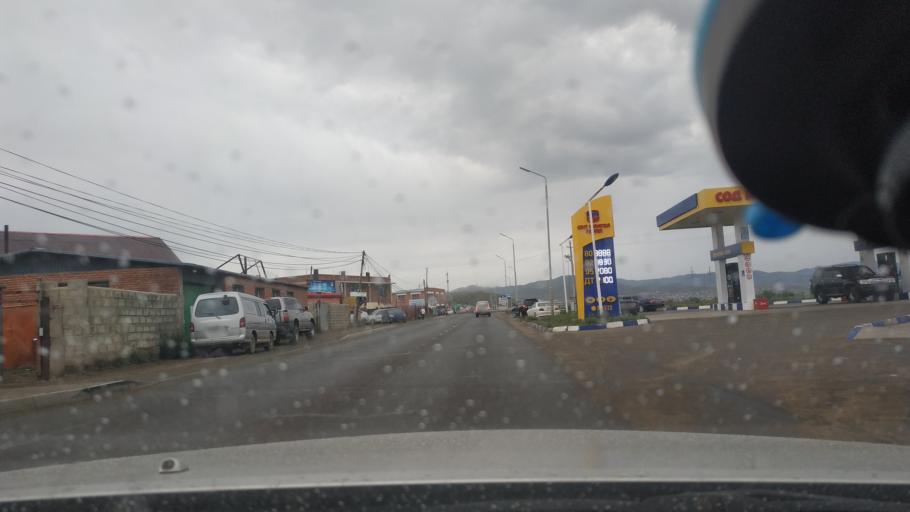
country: MN
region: Ulaanbaatar
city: Ulaanbaatar
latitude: 47.9077
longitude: 107.0353
